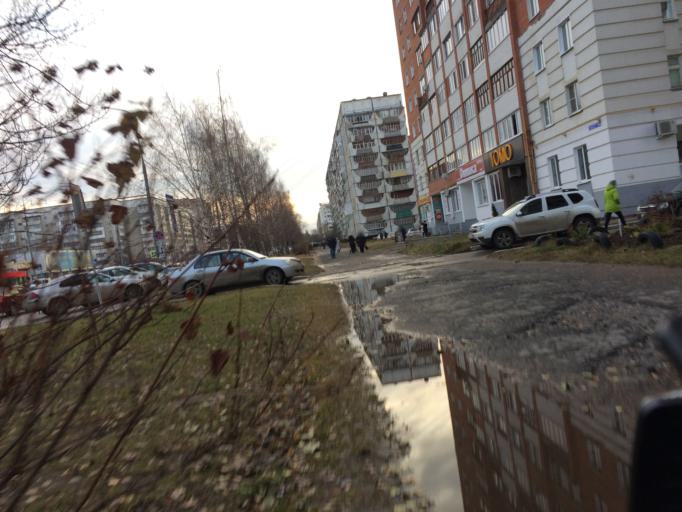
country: RU
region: Mariy-El
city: Yoshkar-Ola
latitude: 56.6338
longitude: 47.9196
